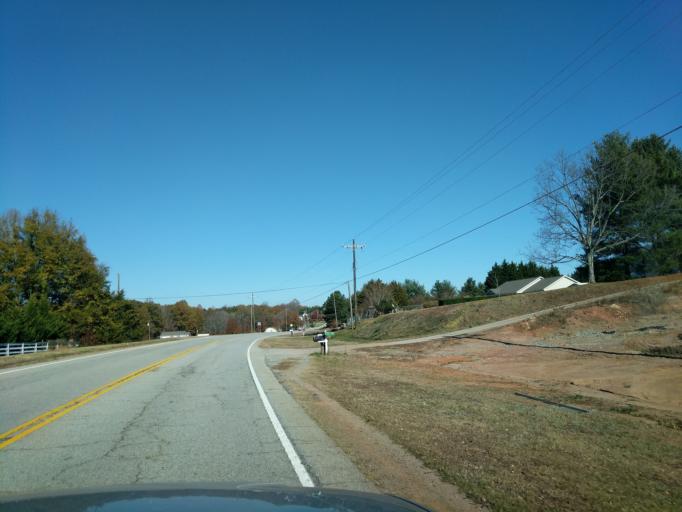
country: US
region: South Carolina
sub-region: Spartanburg County
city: Inman Mills
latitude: 35.0372
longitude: -82.1851
